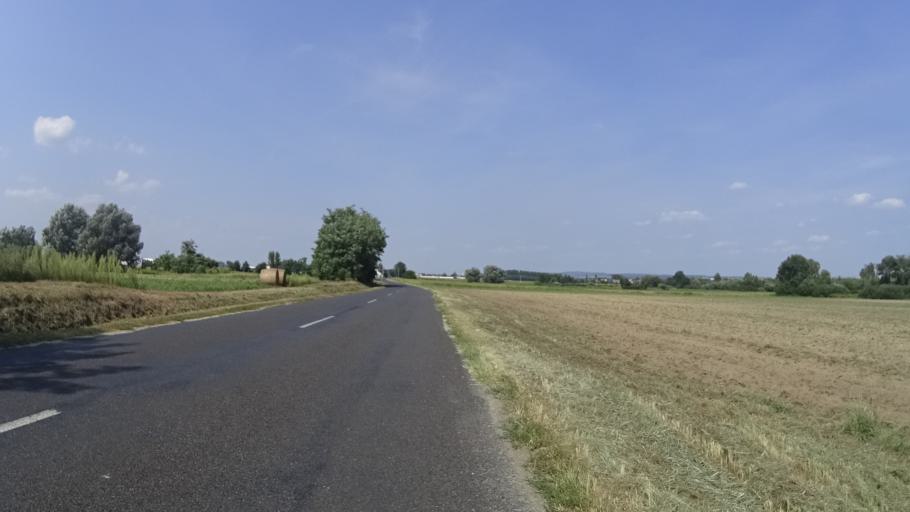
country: HU
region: Zala
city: Nagykanizsa
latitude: 46.4356
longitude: 16.9540
